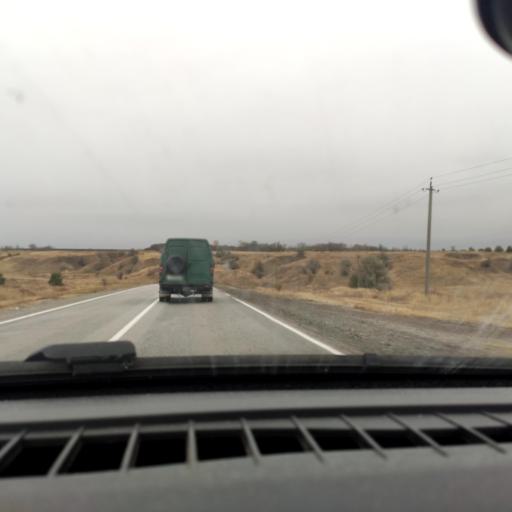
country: RU
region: Voronezj
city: Uryv-Pokrovka
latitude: 51.0694
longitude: 38.9956
